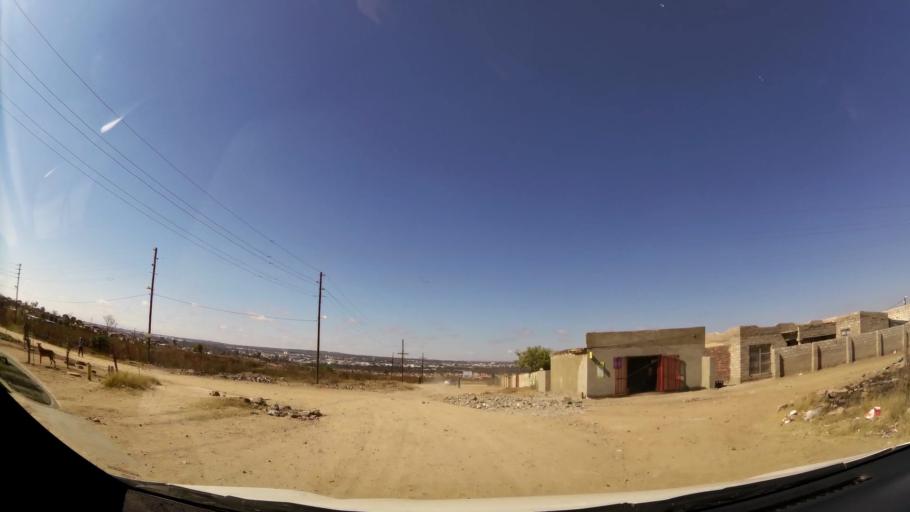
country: ZA
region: Limpopo
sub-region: Capricorn District Municipality
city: Polokwane
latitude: -23.8866
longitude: 29.4111
